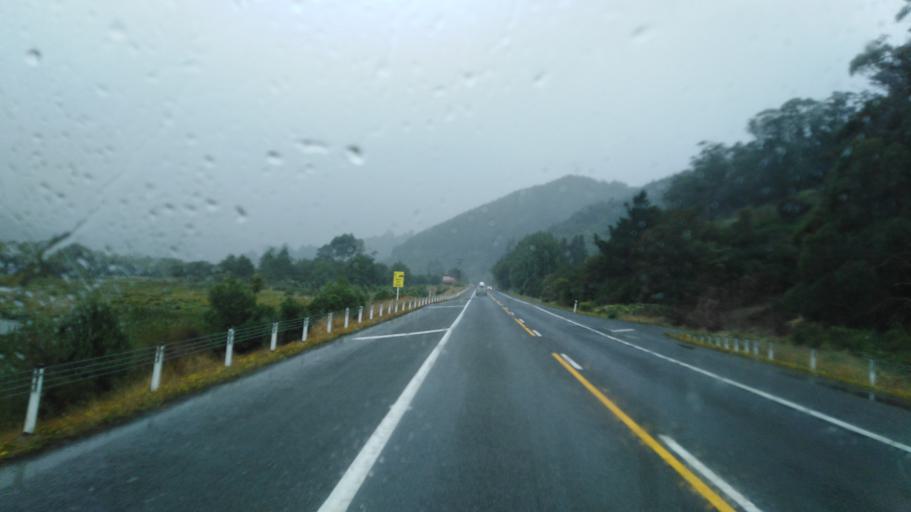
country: NZ
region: Marlborough
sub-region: Marlborough District
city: Picton
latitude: -41.3919
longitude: 173.9511
